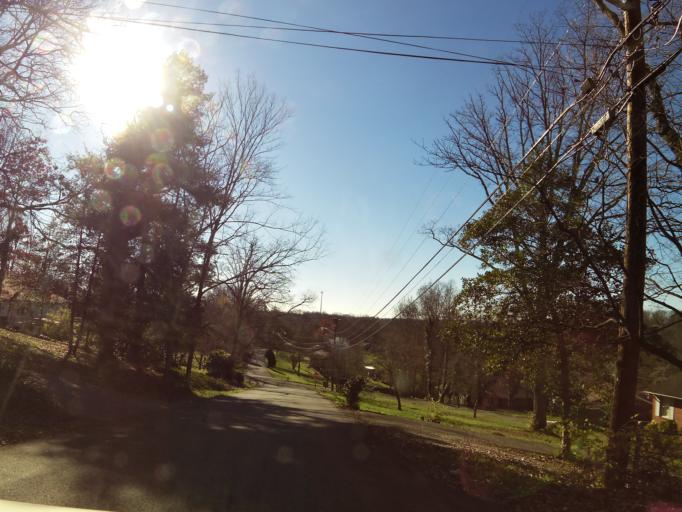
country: US
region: Tennessee
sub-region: Knox County
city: Knoxville
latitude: 36.0300
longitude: -83.9601
